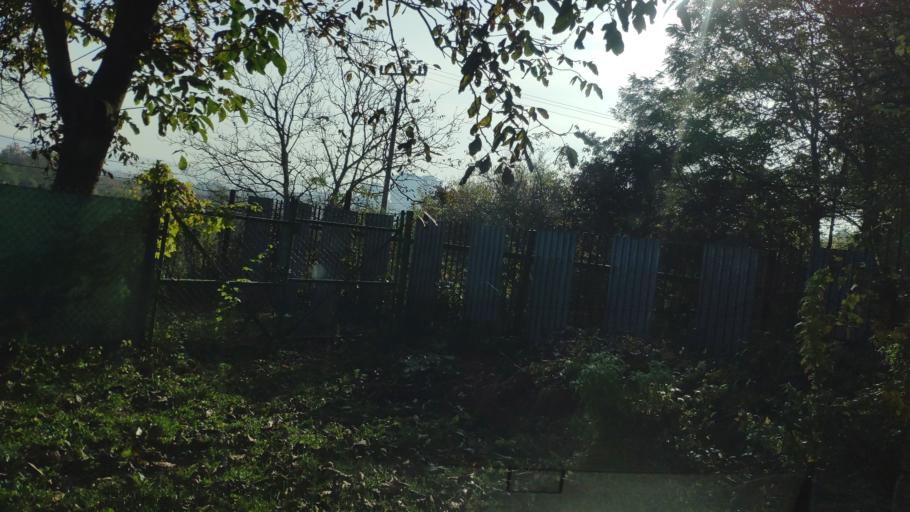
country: SK
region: Kosicky
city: Kosice
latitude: 48.7257
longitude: 21.2239
